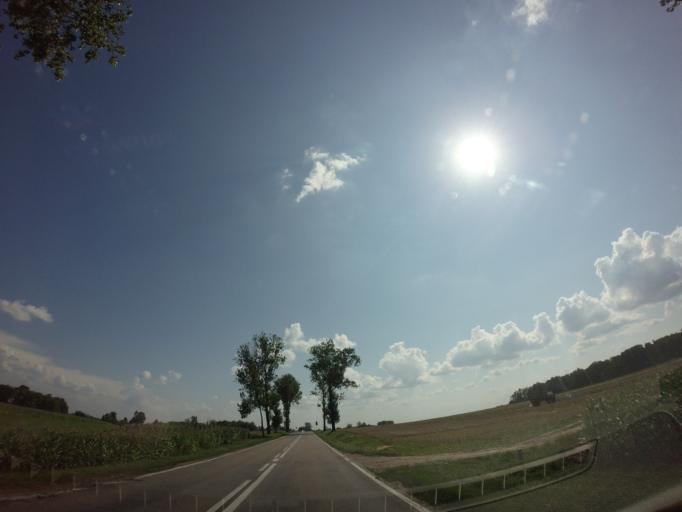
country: PL
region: Podlasie
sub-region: Powiat zambrowski
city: Zambrow
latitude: 52.8928
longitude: 22.2513
